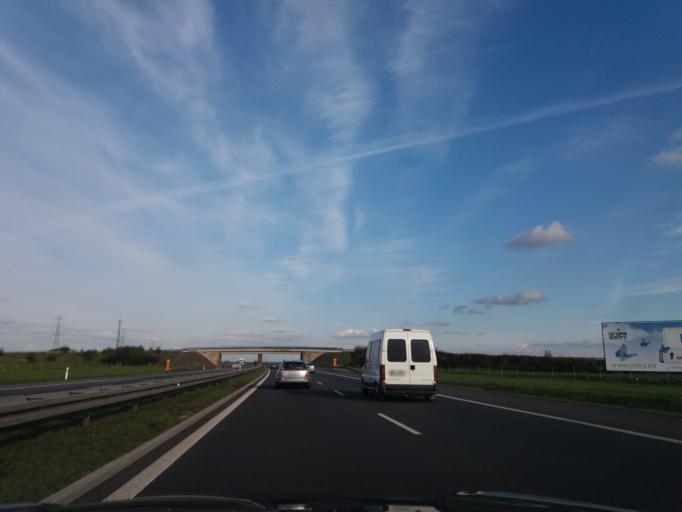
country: PL
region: Opole Voivodeship
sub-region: Powiat brzeski
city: Olszanka
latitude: 50.7389
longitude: 17.4681
